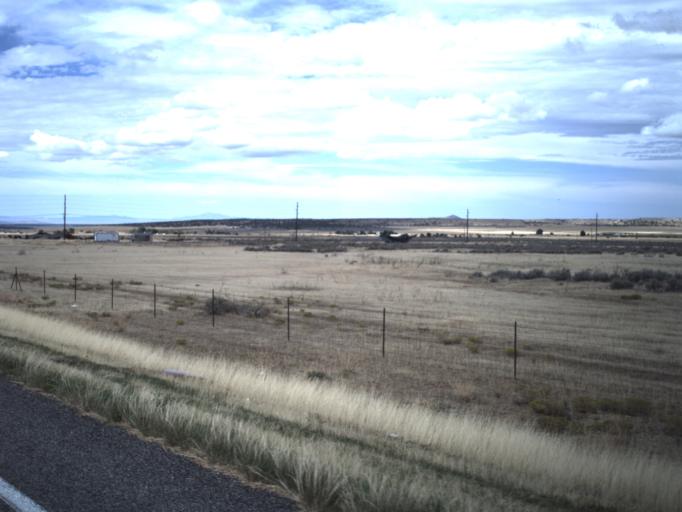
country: US
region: Utah
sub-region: Millard County
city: Fillmore
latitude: 38.9792
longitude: -112.3494
